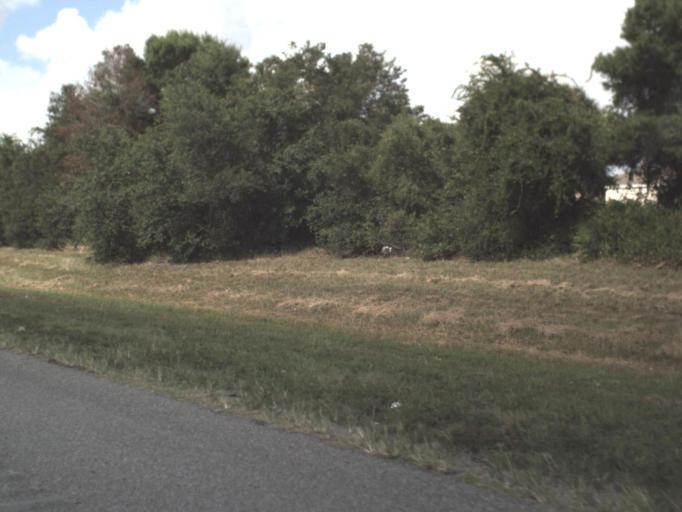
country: US
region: Florida
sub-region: Hillsborough County
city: Riverview
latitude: 27.8416
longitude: -82.3484
